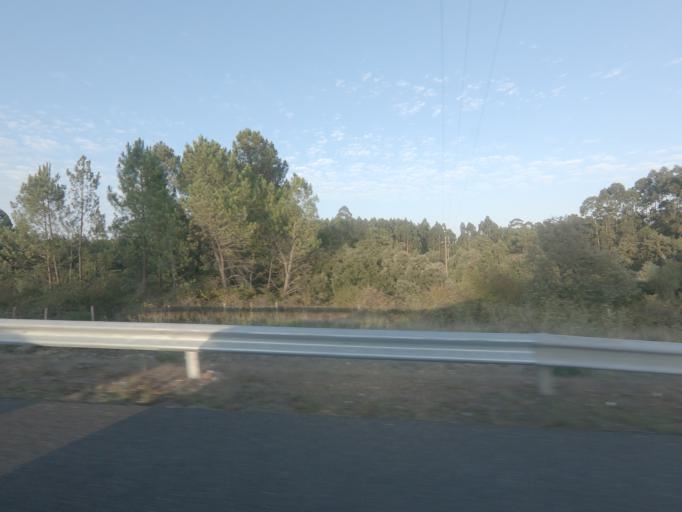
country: PT
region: Leiria
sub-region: Leiria
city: Santa Catarina da Serra
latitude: 39.6387
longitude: -8.6988
